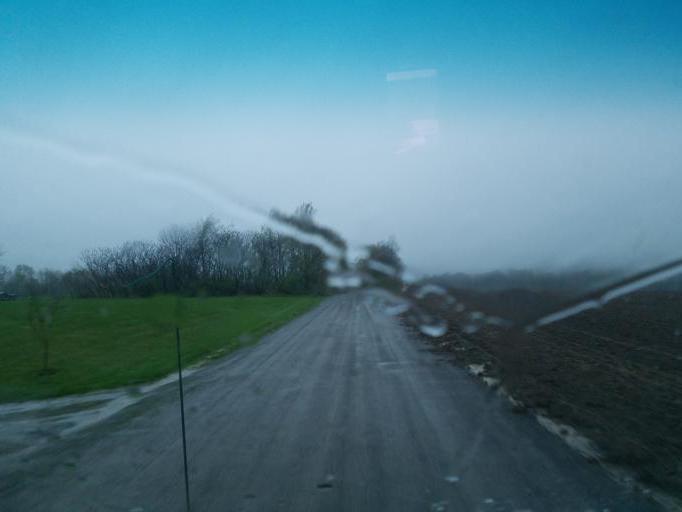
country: US
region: Pennsylvania
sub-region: Tioga County
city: Westfield
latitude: 41.9206
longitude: -77.7275
